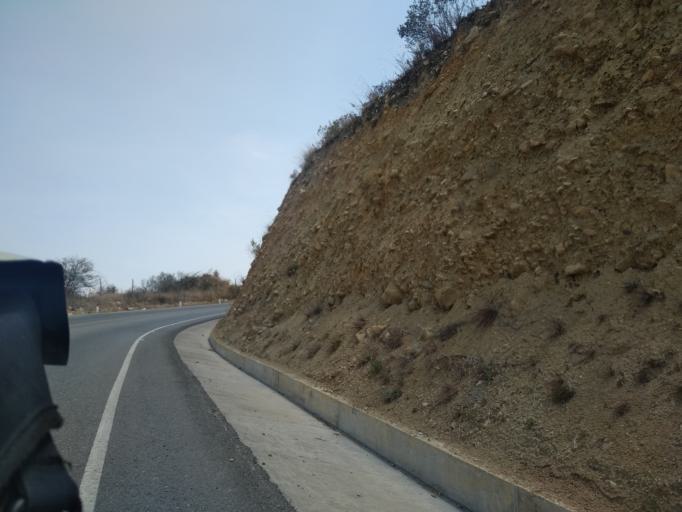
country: PE
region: Cajamarca
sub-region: Provincia de Cajabamba
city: Cauday
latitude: -7.6136
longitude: -78.0855
